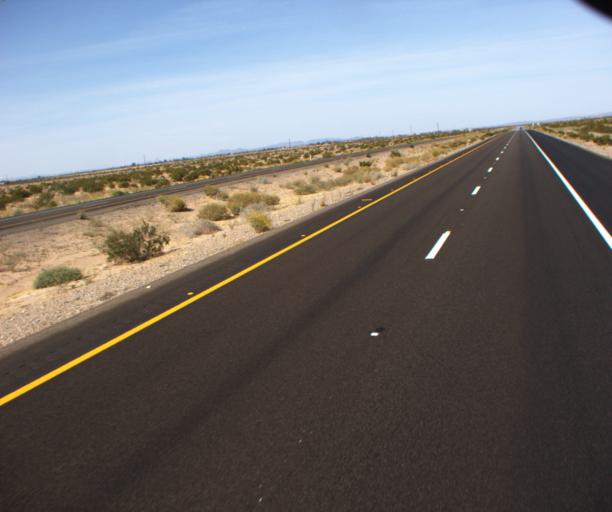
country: US
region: Arizona
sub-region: Yuma County
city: Somerton
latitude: 32.5728
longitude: -114.5557
